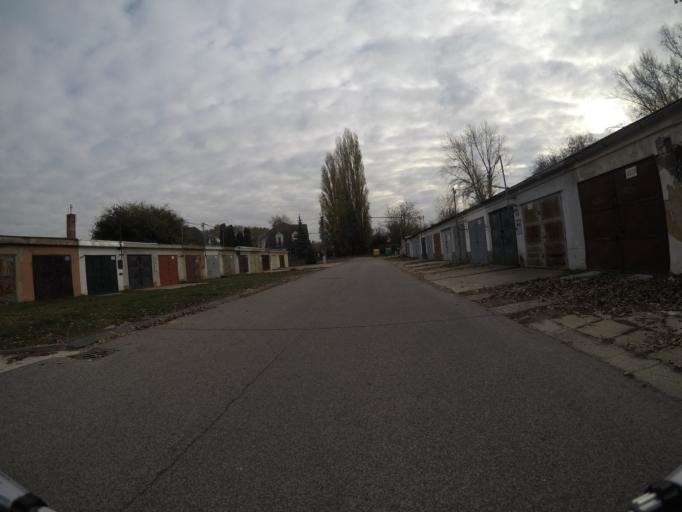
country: SK
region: Bratislavsky
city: Bratislava
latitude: 48.1668
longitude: 17.1598
